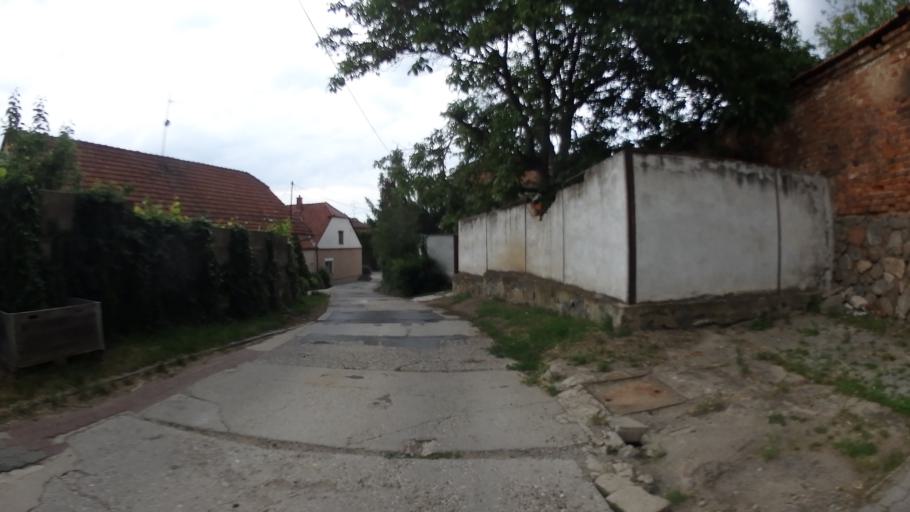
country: CZ
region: South Moravian
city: Ostopovice
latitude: 49.1408
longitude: 16.5513
